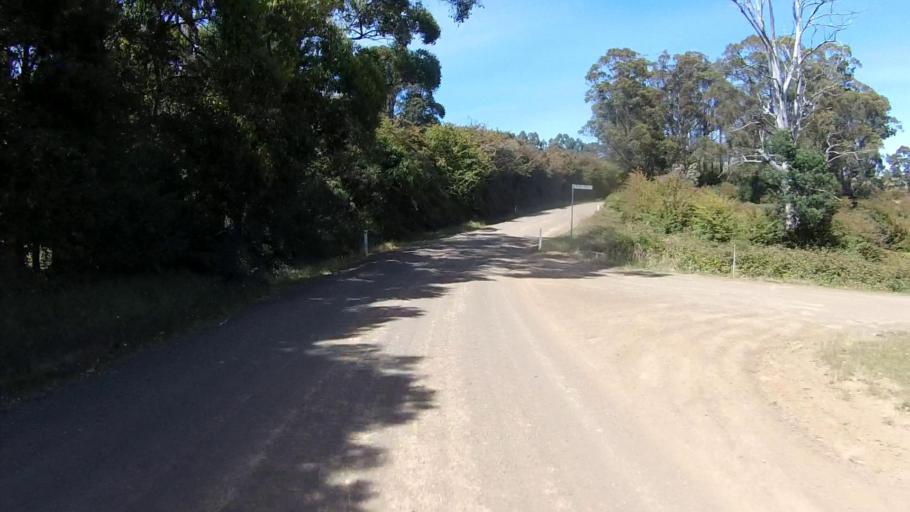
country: AU
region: Tasmania
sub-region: Sorell
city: Sorell
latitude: -42.7172
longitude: 147.7514
